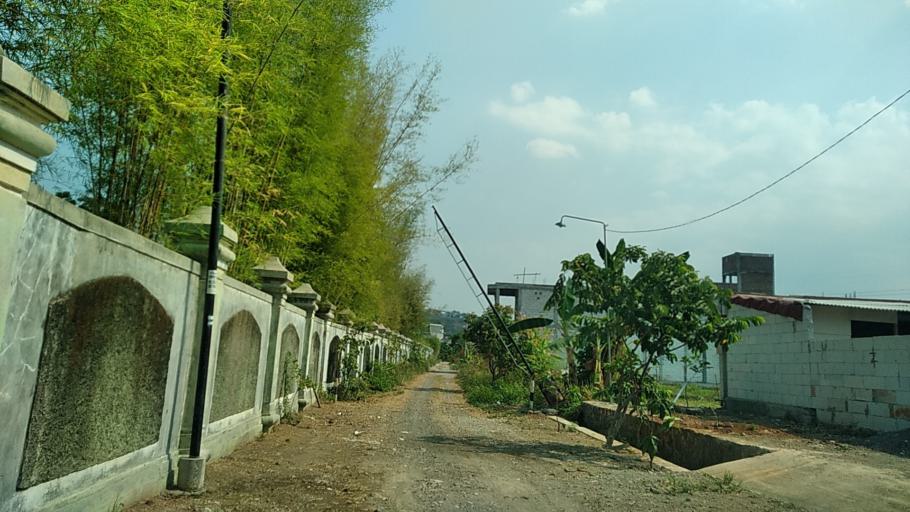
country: ID
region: Central Java
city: Mranggen
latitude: -7.0329
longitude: 110.4645
